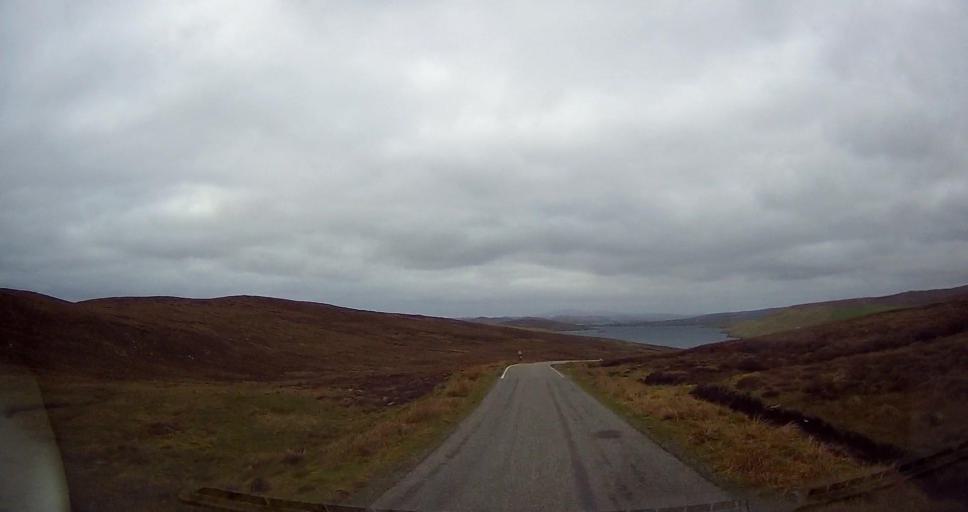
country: GB
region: Scotland
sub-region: Shetland Islands
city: Lerwick
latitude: 60.3231
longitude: -1.3384
